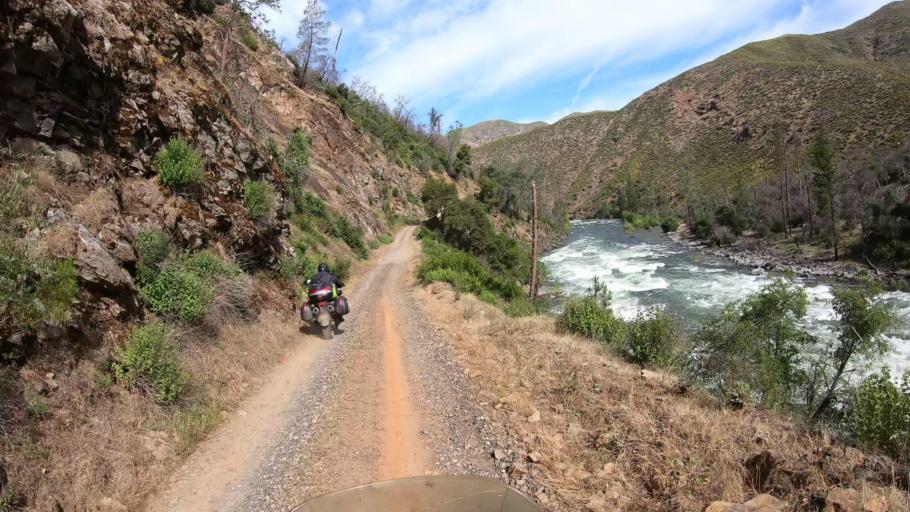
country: US
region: California
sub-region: Tuolumne County
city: Tuolumne City
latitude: 37.8353
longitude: -120.0567
